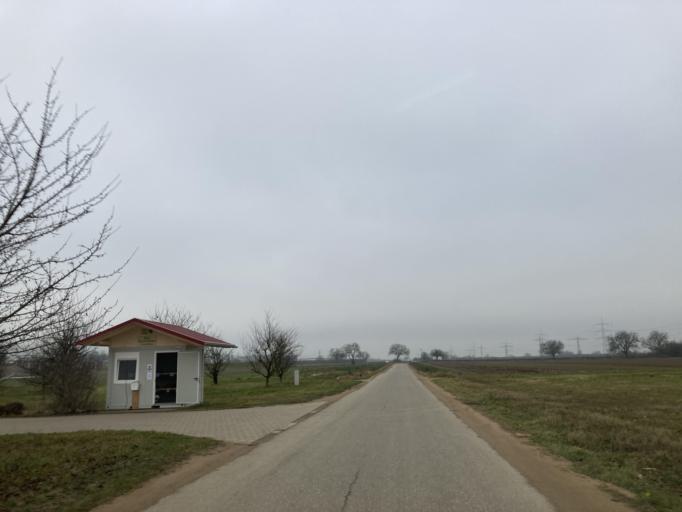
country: DE
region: Baden-Wuerttemberg
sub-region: Freiburg Region
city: Auggen
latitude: 47.7954
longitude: 7.5873
